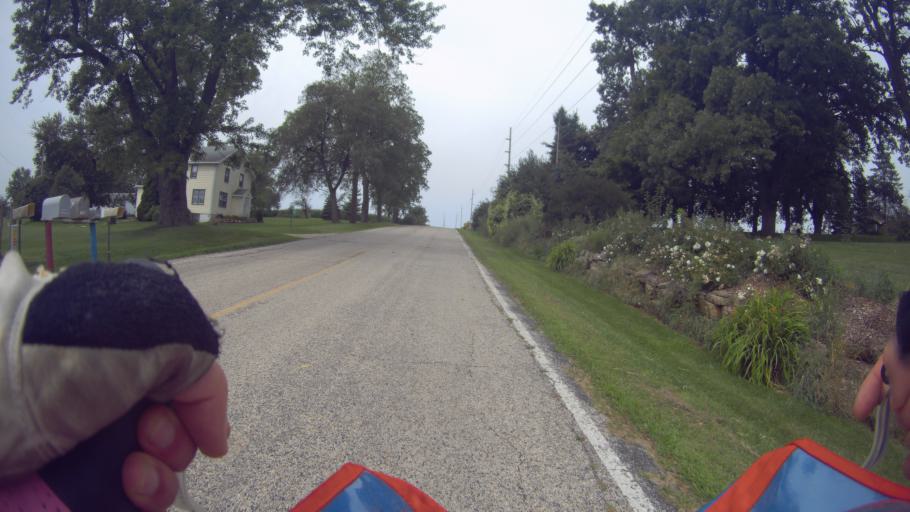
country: US
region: Wisconsin
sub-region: Dane County
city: Verona
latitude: 42.9732
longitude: -89.5695
